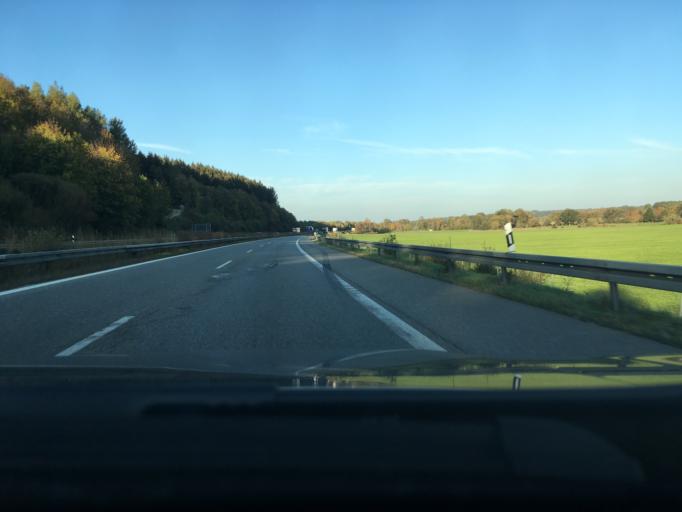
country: DE
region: Baden-Wuerttemberg
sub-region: Tuebingen Region
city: Aitrach
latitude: 47.9151
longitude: 10.0701
